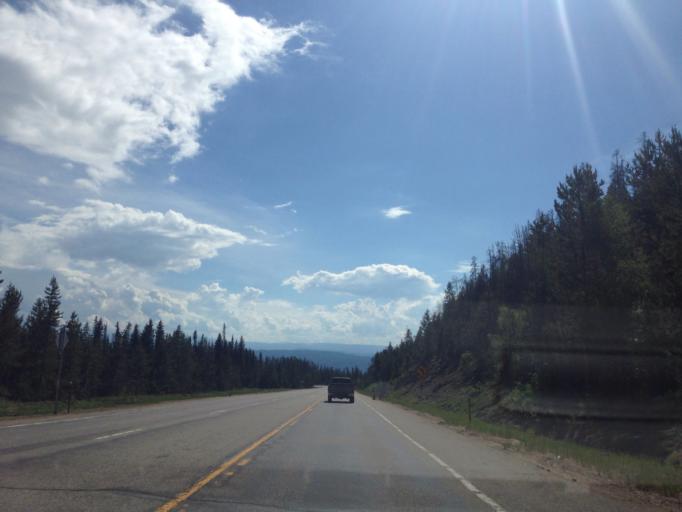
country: US
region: Colorado
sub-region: Routt County
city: Steamboat Springs
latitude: 40.3660
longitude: -106.7458
